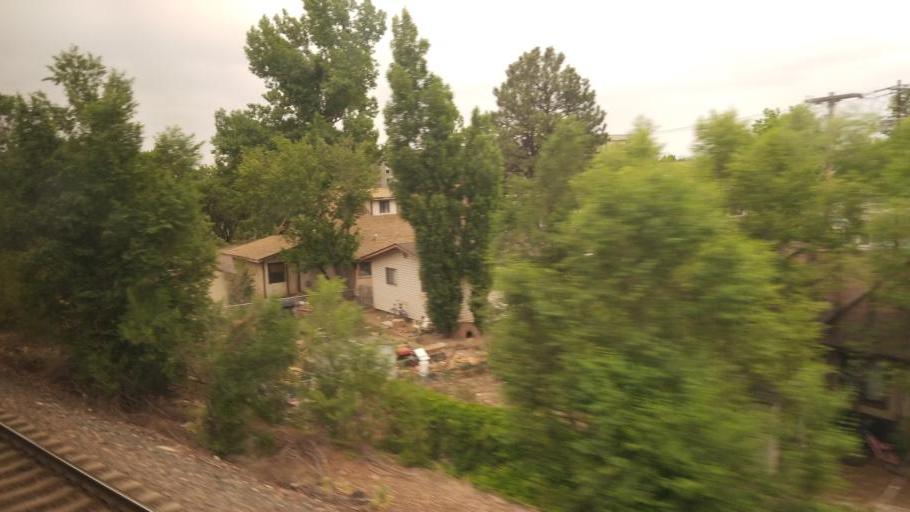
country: US
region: Arizona
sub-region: Coconino County
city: Flagstaff
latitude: 35.1981
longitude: -111.6553
